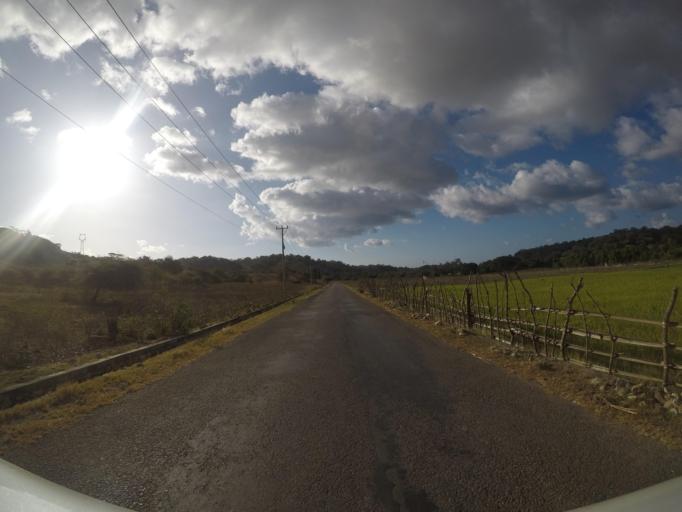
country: TL
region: Lautem
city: Lospalos
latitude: -8.4219
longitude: 126.8301
